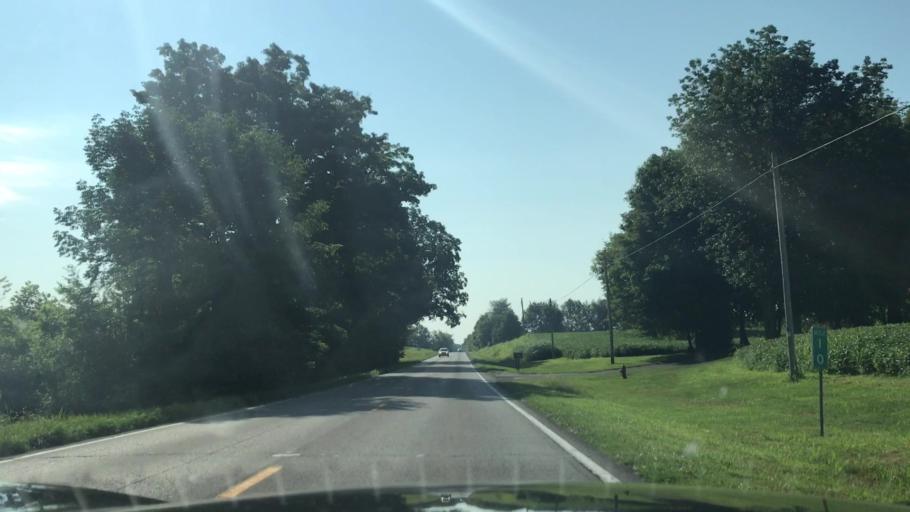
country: US
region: Kentucky
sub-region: Hart County
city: Horse Cave
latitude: 37.1733
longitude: -85.8614
